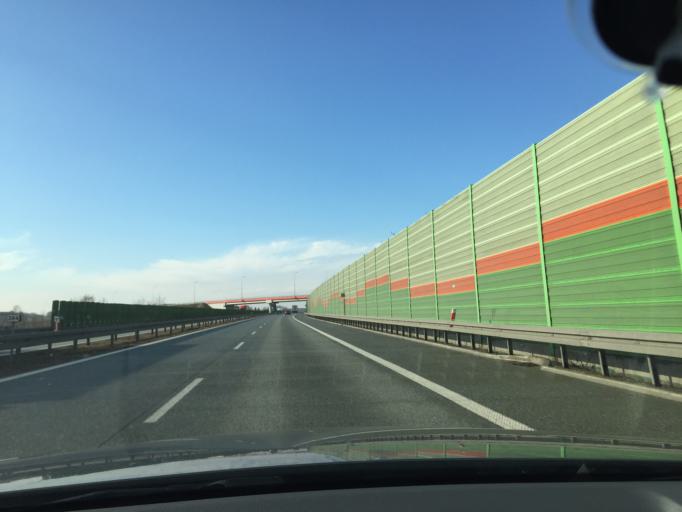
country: PL
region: Lodz Voivodeship
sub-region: Powiat rawski
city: Rawa Mazowiecka
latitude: 51.7580
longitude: 20.2597
